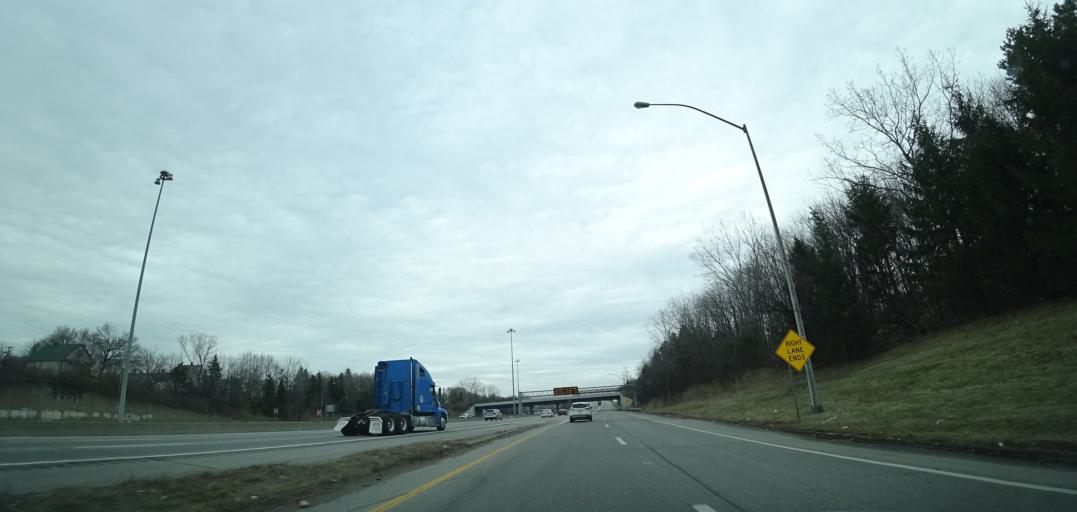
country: US
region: Ohio
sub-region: Cuyahoga County
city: Brooklyn
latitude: 41.4700
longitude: -81.7385
